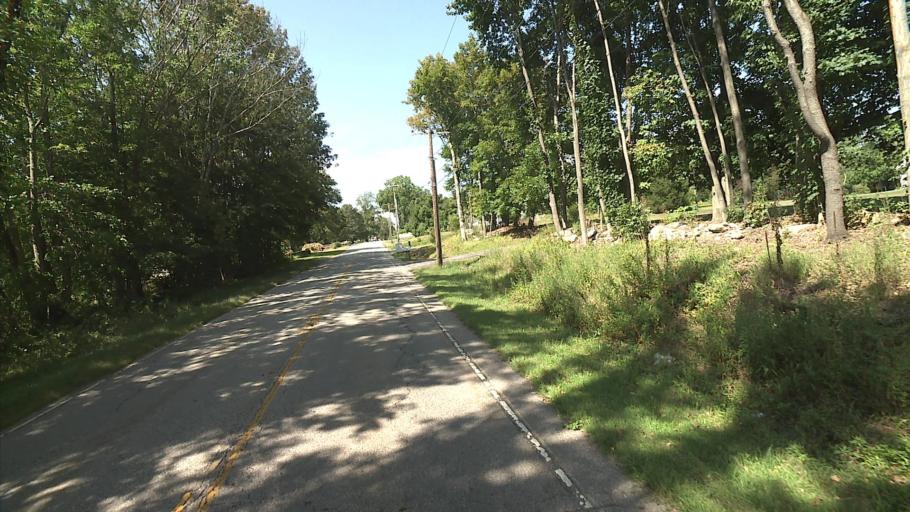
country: US
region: Connecticut
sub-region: Windham County
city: Willimantic
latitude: 41.6622
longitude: -72.2519
